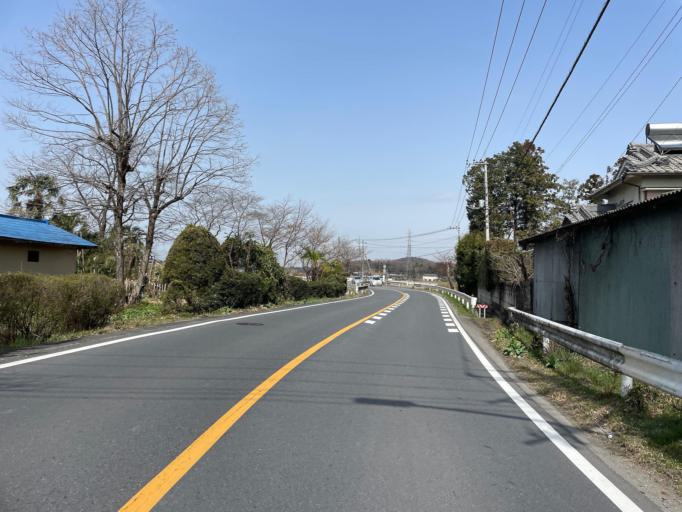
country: JP
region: Saitama
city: Ogawa
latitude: 36.0726
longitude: 139.2961
